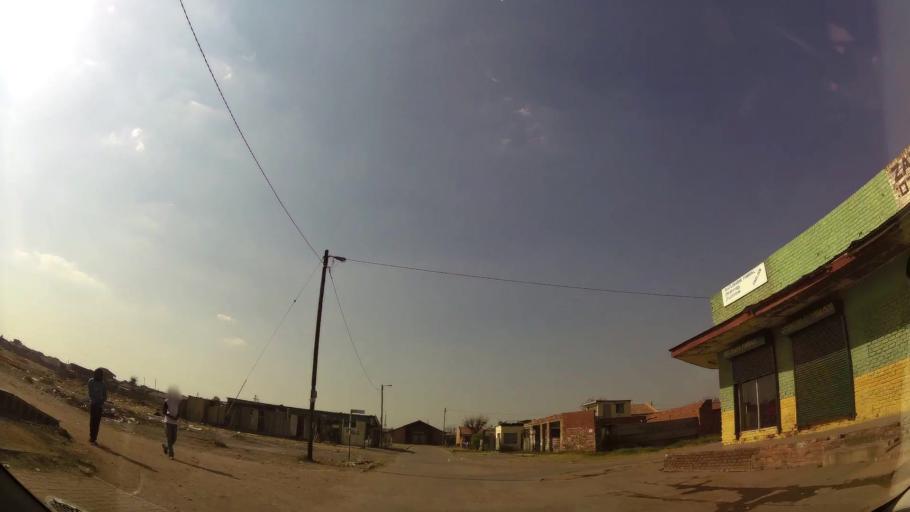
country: ZA
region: Gauteng
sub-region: Ekurhuleni Metropolitan Municipality
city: Brakpan
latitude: -26.1404
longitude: 28.4190
